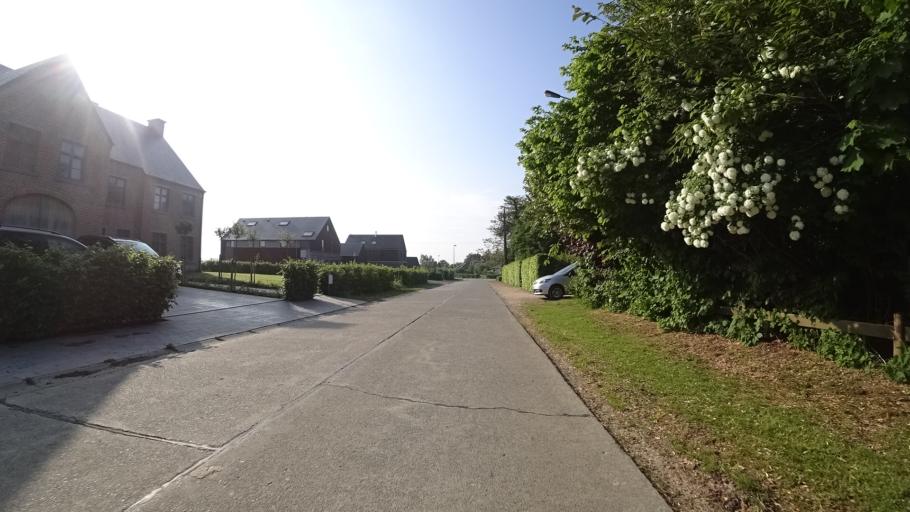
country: BE
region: Wallonia
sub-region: Province de Namur
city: Namur
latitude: 50.5218
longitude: 4.8248
